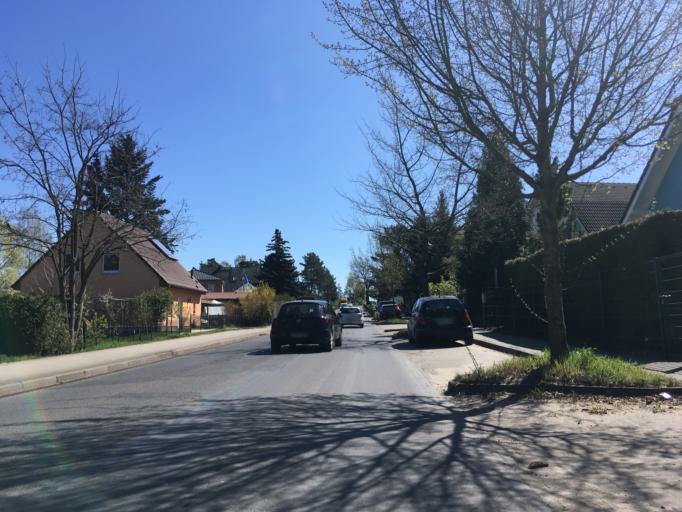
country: DE
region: Brandenburg
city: Bernau bei Berlin
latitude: 52.6455
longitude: 13.5545
